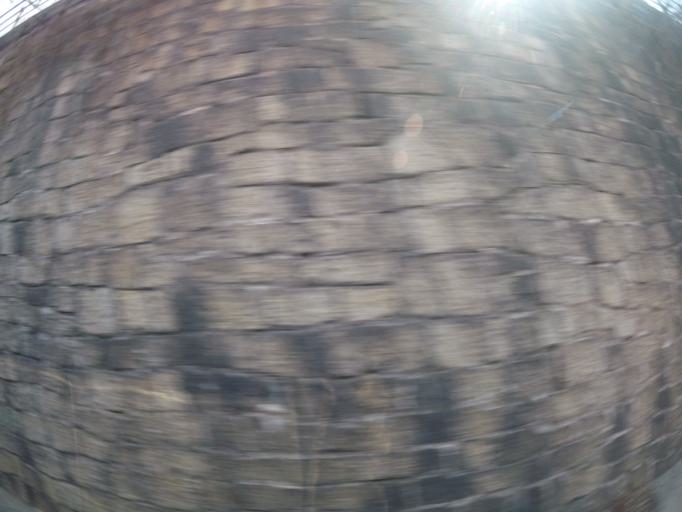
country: IT
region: Piedmont
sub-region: Provincia Verbano-Cusio-Ossola
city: Nonio
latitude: 45.8450
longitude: 8.4053
